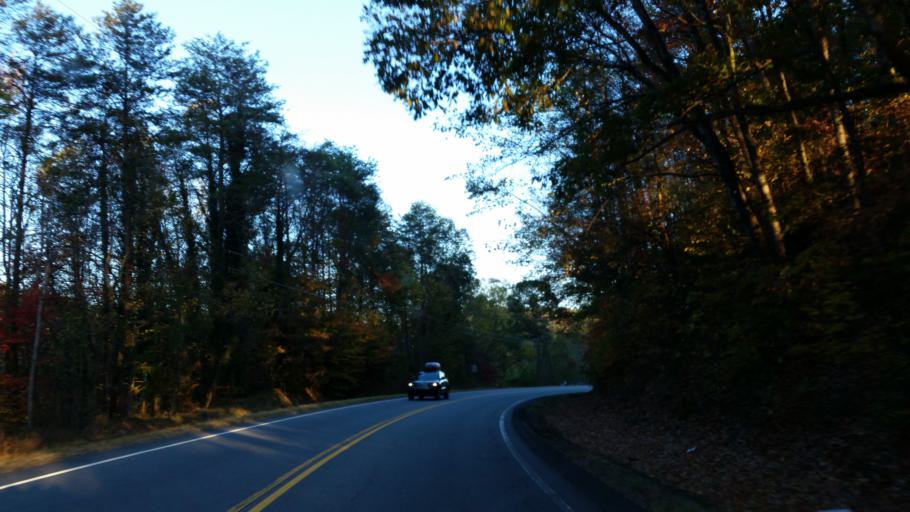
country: US
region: Georgia
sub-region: Lumpkin County
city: Dahlonega
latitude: 34.5325
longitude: -84.0093
